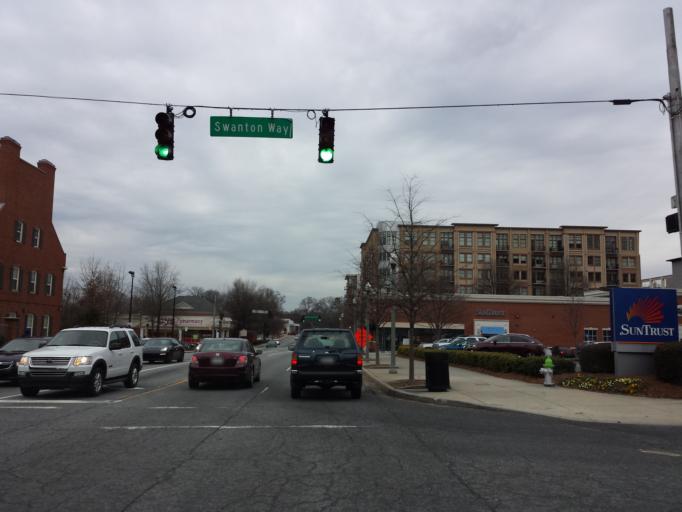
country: US
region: Georgia
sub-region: DeKalb County
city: Decatur
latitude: 33.7747
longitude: -84.2988
